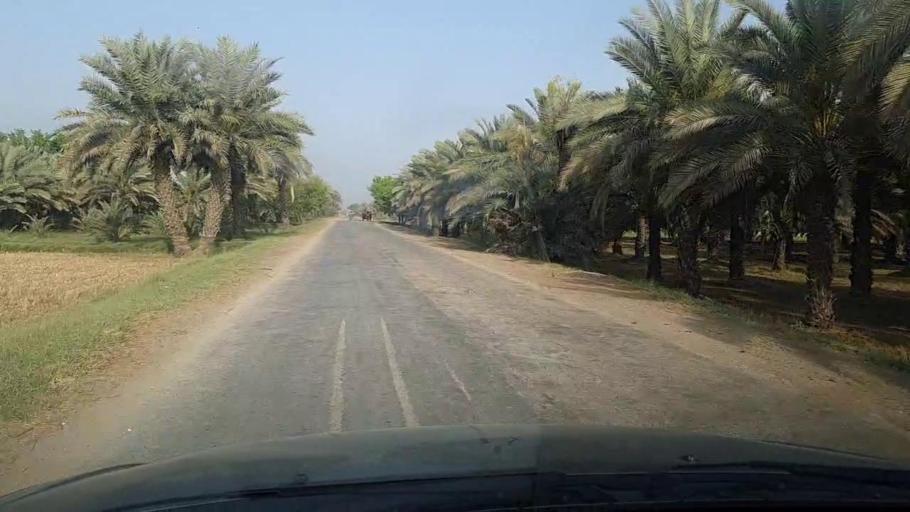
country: PK
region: Sindh
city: Pir jo Goth
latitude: 27.5641
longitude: 68.6499
